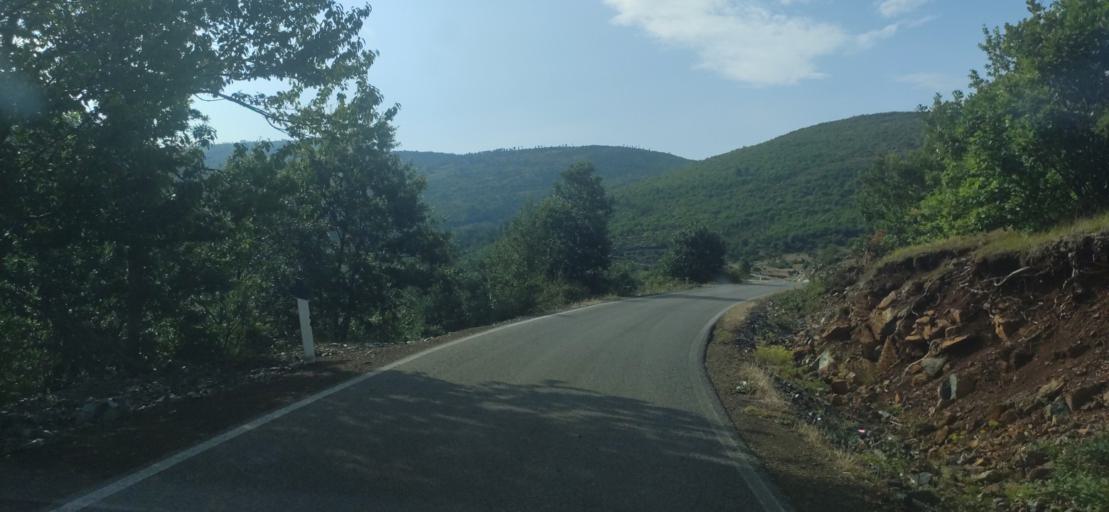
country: AL
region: Shkoder
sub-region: Rrethi i Pukes
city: Iballe
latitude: 42.1805
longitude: 20.0005
